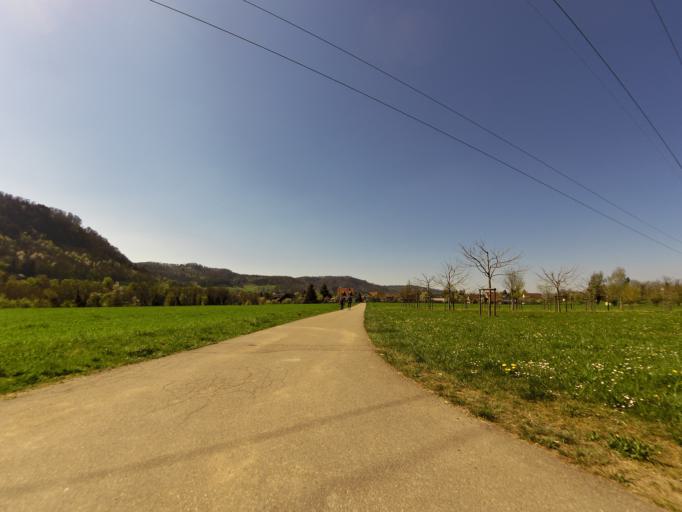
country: CH
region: Aargau
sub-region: Bezirk Zurzach
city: Bad Zurzach
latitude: 47.5718
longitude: 8.3364
